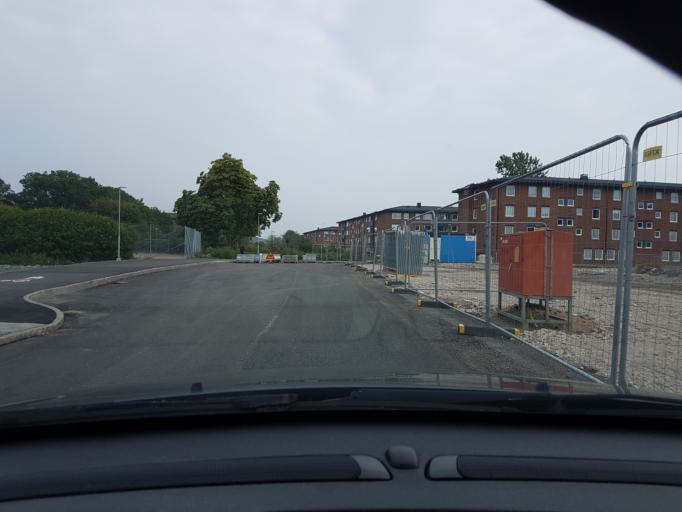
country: SE
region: Vaestra Goetaland
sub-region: Goteborg
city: Majorna
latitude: 57.6416
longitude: 11.9014
